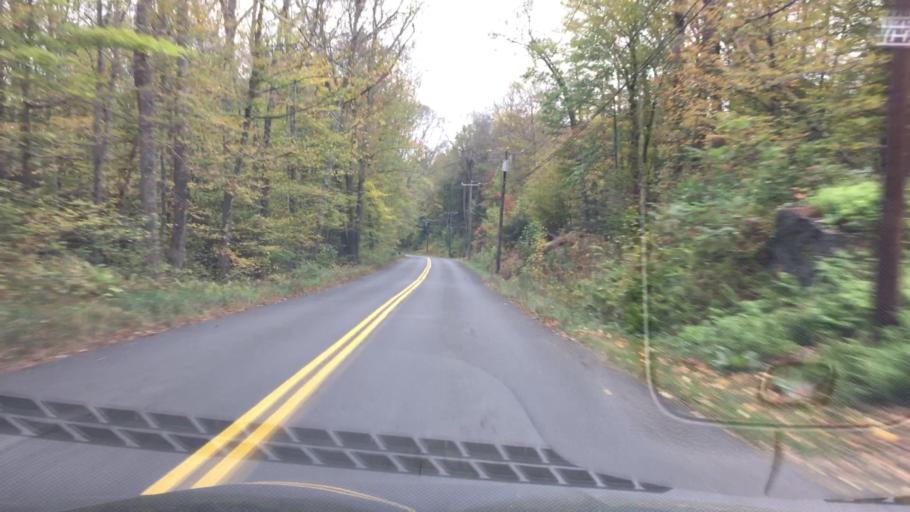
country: US
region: Connecticut
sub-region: Tolland County
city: Somers
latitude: 41.9687
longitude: -72.4133
